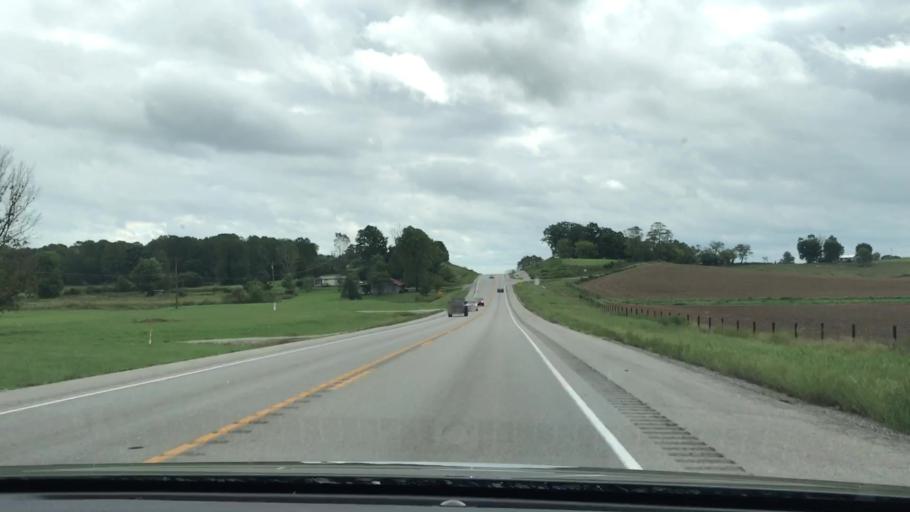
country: US
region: Kentucky
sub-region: Barren County
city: Glasgow
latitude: 36.9520
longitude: -85.8512
